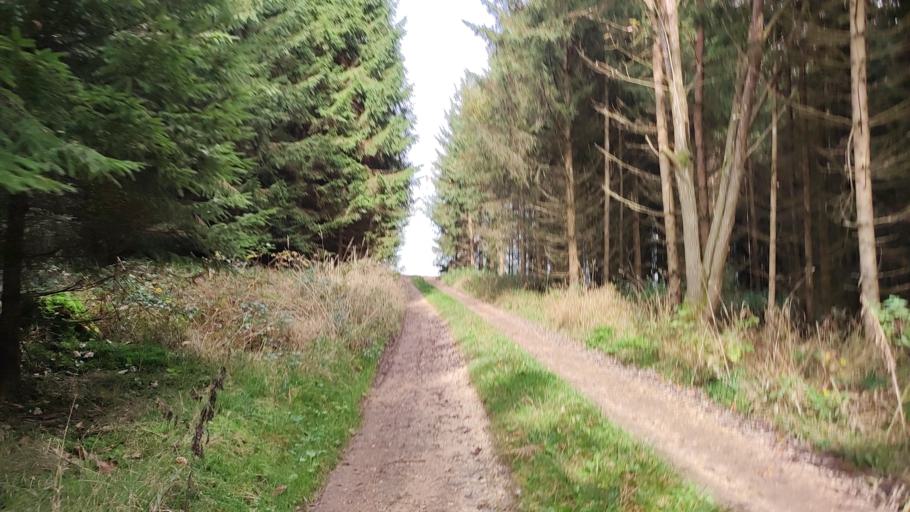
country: DE
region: Bavaria
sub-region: Swabia
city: Ziemetshausen
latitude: 48.2773
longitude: 10.5634
